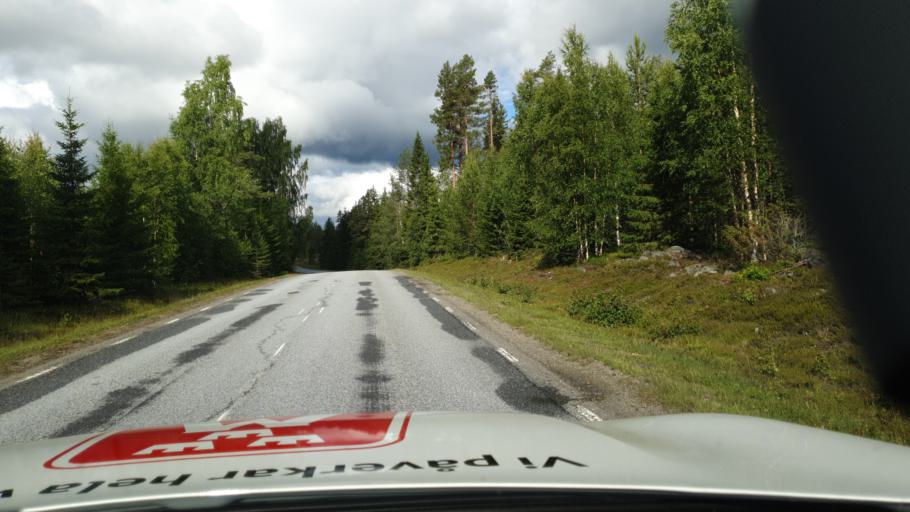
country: SE
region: Vaesterbotten
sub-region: Umea Kommun
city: Hoernefors
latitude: 63.6815
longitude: 20.0457
